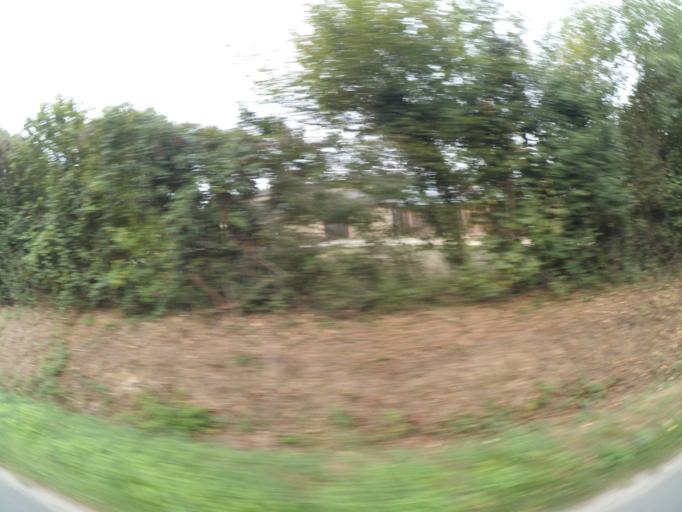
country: FR
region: Pays de la Loire
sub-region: Departement de la Vendee
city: Saint-Andre-Treize-Voies
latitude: 46.9317
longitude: -1.4031
